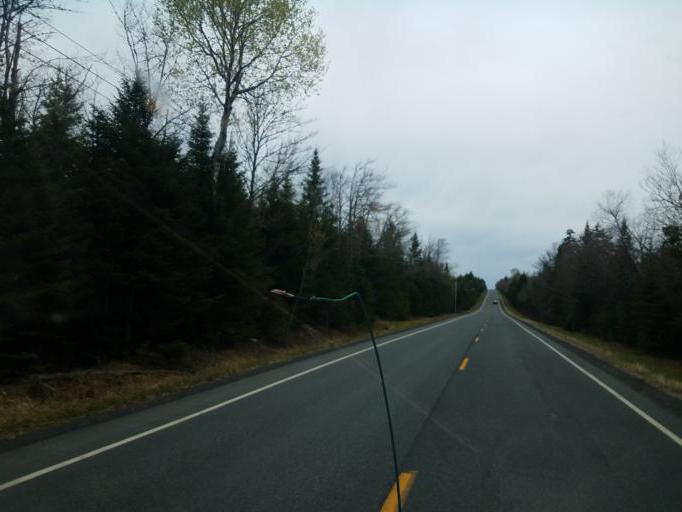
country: US
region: Maine
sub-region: Penobscot County
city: Patten
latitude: 46.2908
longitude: -68.3577
